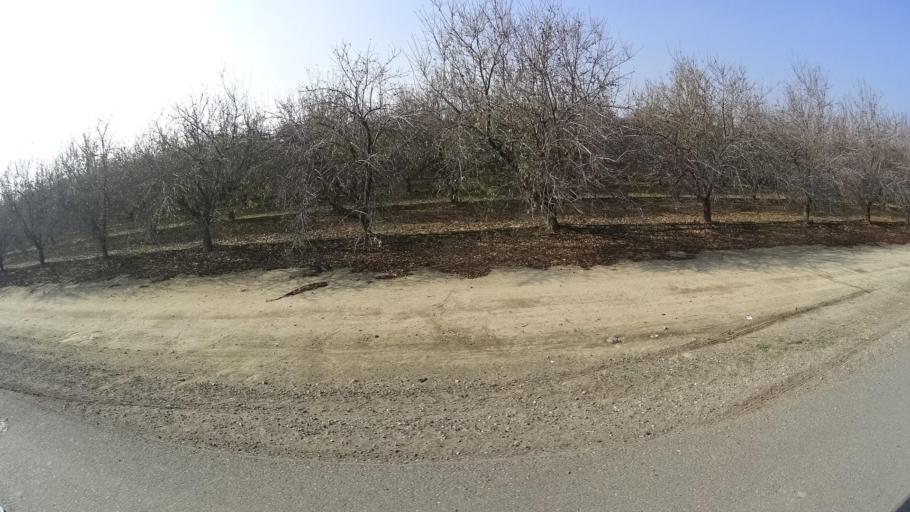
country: US
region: California
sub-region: Kern County
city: Greenfield
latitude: 35.2552
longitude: -119.1098
